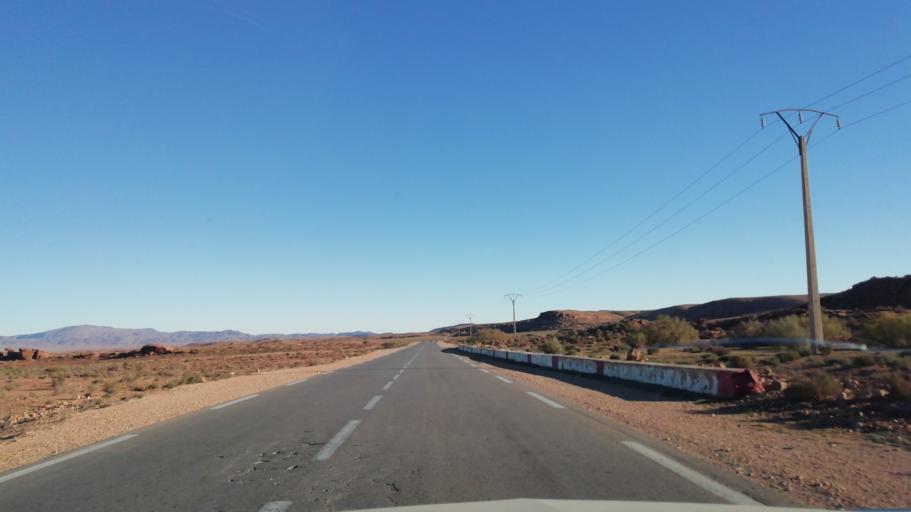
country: DZ
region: El Bayadh
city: El Abiodh Sidi Cheikh
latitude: 33.1708
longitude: 0.4577
